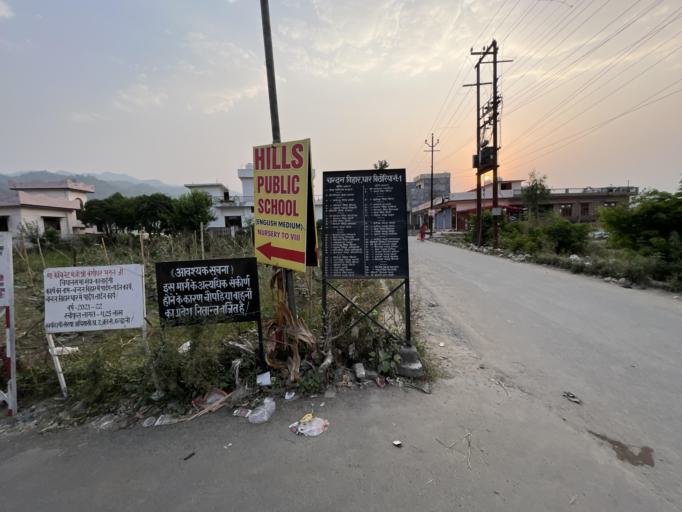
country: IN
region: Uttarakhand
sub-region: Naini Tal
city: Haldwani
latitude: 29.2312
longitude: 79.5060
